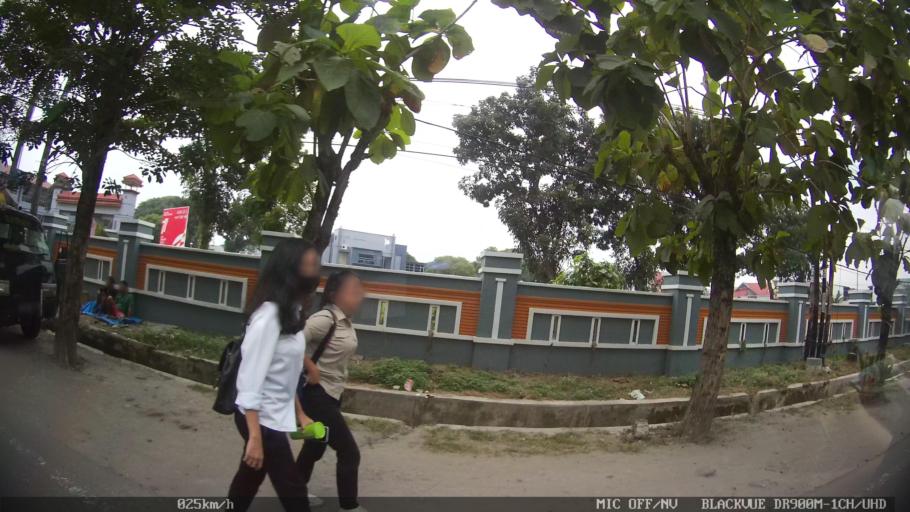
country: ID
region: North Sumatra
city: Medan
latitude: 3.5601
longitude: 98.7198
